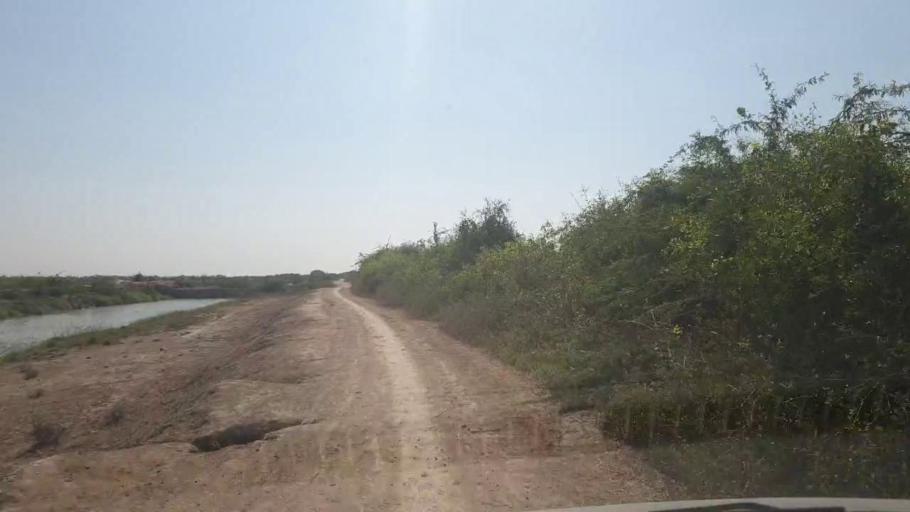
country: PK
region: Sindh
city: Tando Bago
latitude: 24.9147
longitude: 69.1645
